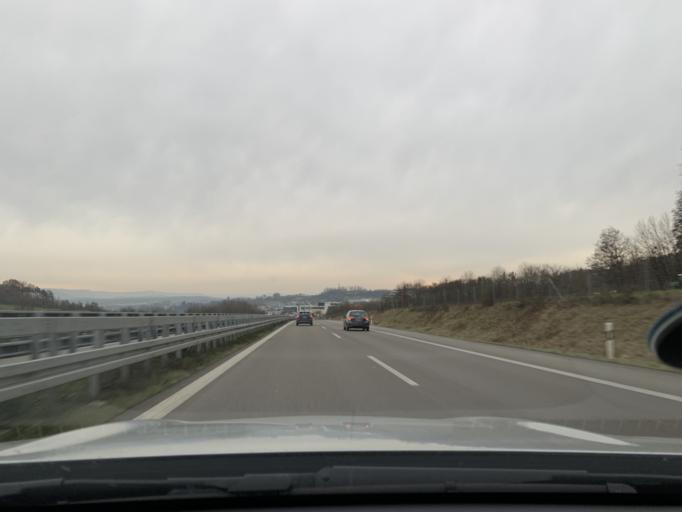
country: DE
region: Baden-Wuerttemberg
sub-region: Regierungsbezirk Stuttgart
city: Unterensingen
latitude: 48.6505
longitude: 9.3353
